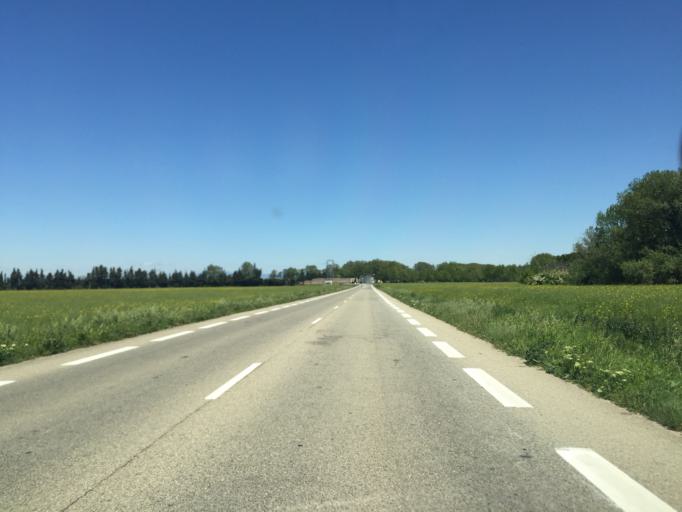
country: FR
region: Provence-Alpes-Cote d'Azur
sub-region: Departement du Vaucluse
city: Jonquieres
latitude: 44.1212
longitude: 4.9295
